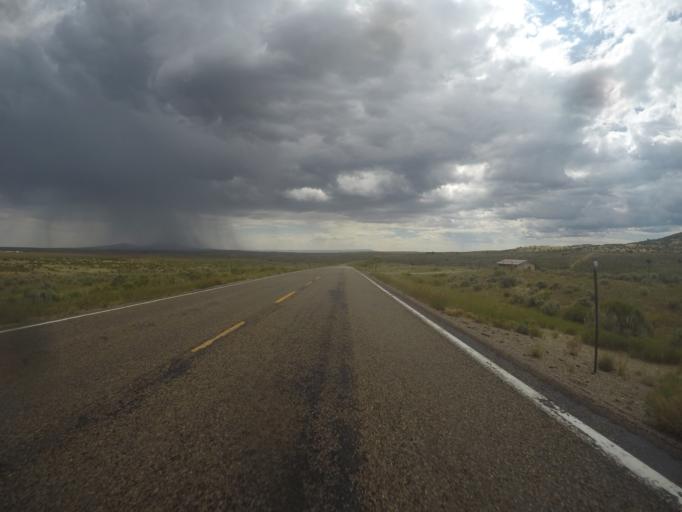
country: US
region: Utah
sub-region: Daggett County
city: Manila
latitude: 41.0269
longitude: -109.8817
